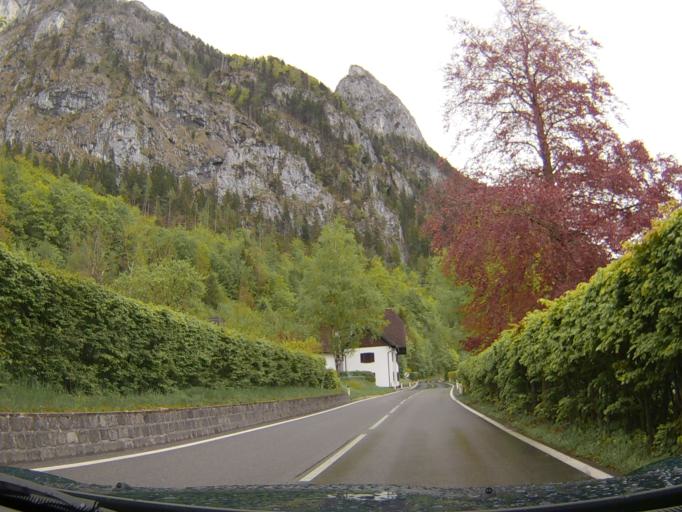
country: AT
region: Upper Austria
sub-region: Politischer Bezirk Vocklabruck
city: Steinbach am Attersee
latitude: 47.8070
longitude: 13.5480
